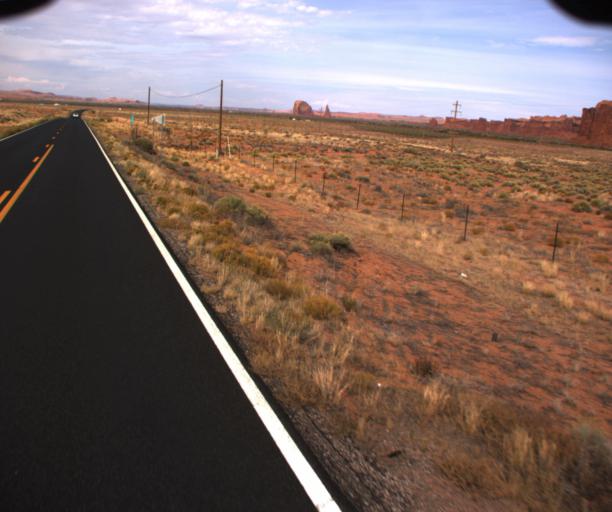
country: US
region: Arizona
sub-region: Apache County
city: Many Farms
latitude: 36.6073
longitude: -109.5743
